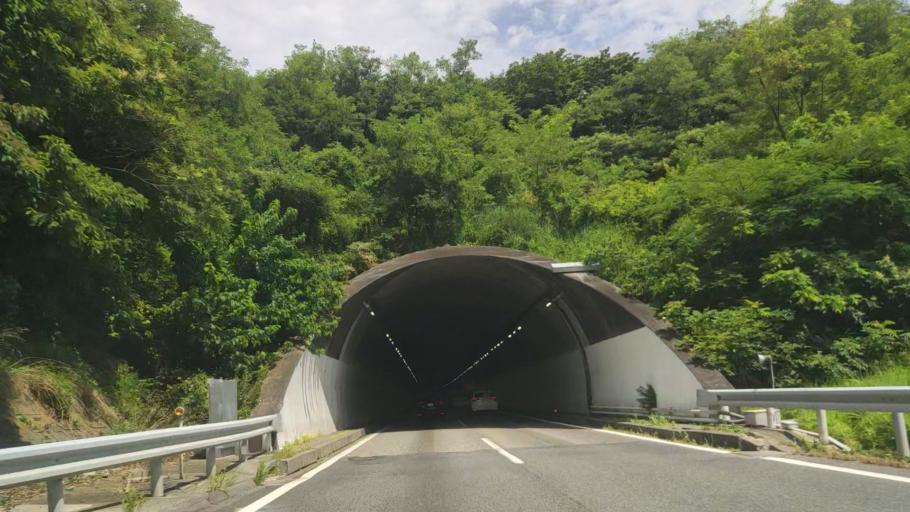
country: JP
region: Gunma
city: Numata
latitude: 36.5824
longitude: 139.0636
